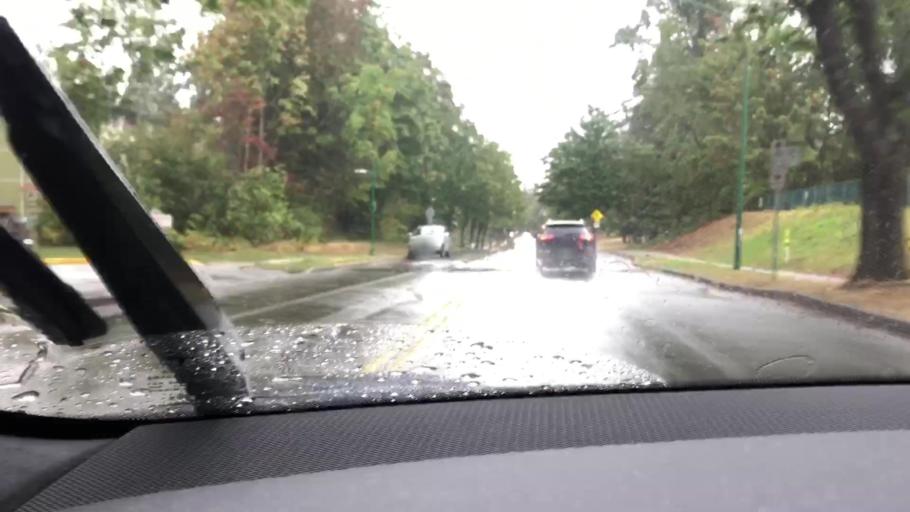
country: CA
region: British Columbia
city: New Westminster
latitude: 49.2336
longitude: -122.9146
